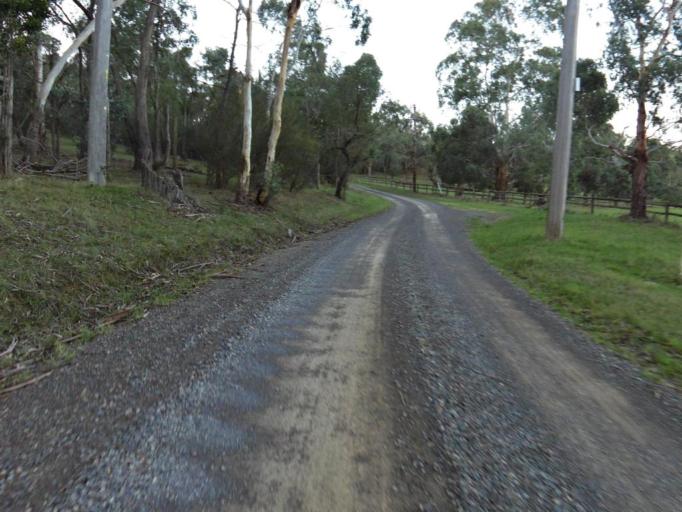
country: AU
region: Victoria
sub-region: Manningham
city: Warrandyte
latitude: -37.7403
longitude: 145.2378
